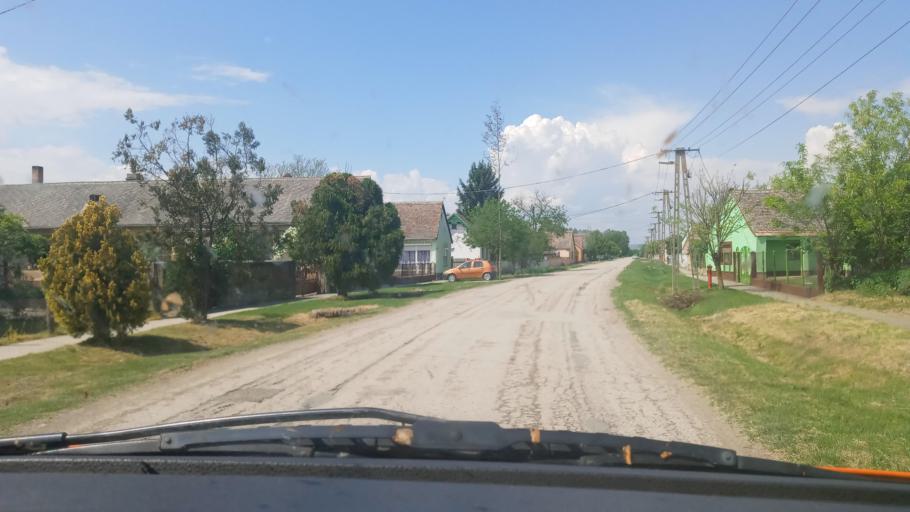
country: HU
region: Baranya
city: Beremend
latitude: 45.7909
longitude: 18.3507
